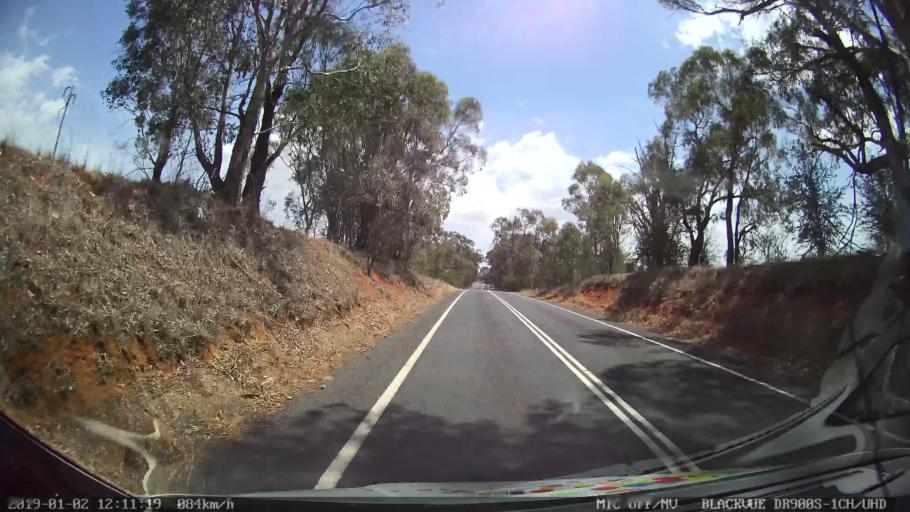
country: AU
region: New South Wales
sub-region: Young
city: Young
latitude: -34.4506
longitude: 148.2576
